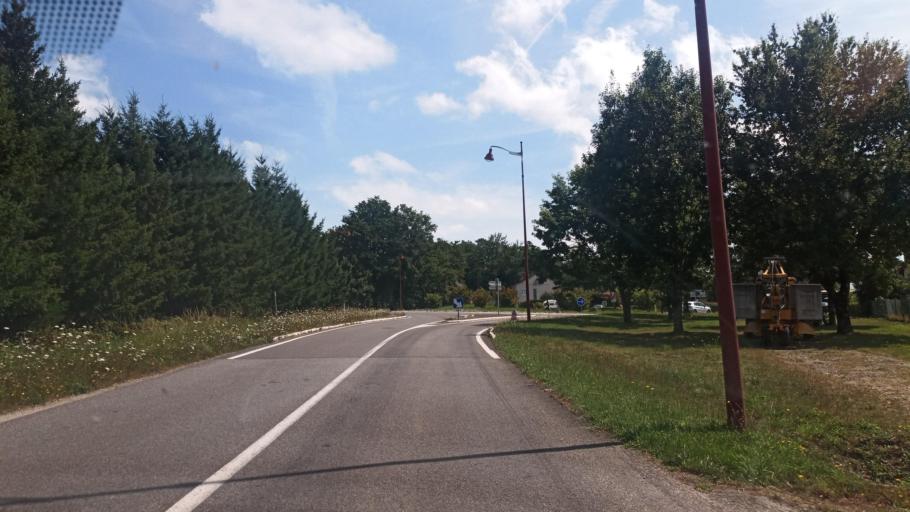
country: FR
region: Limousin
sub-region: Departement de la Haute-Vienne
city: Veyrac
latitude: 45.9001
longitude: 1.0868
